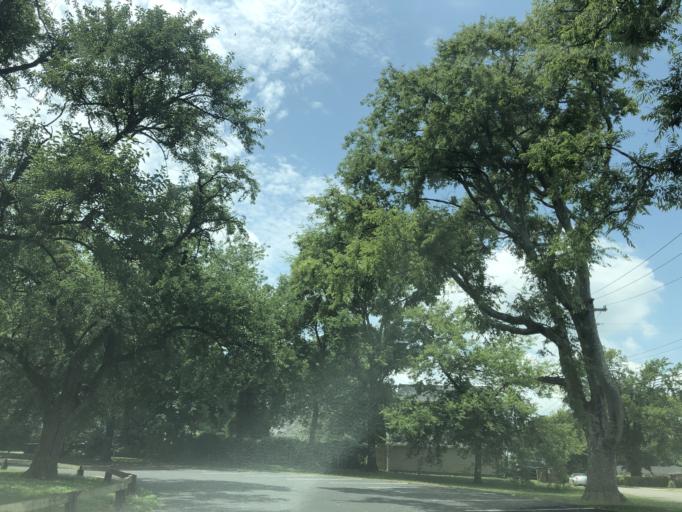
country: US
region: Tennessee
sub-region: Davidson County
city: Nashville
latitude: 36.1650
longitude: -86.8239
